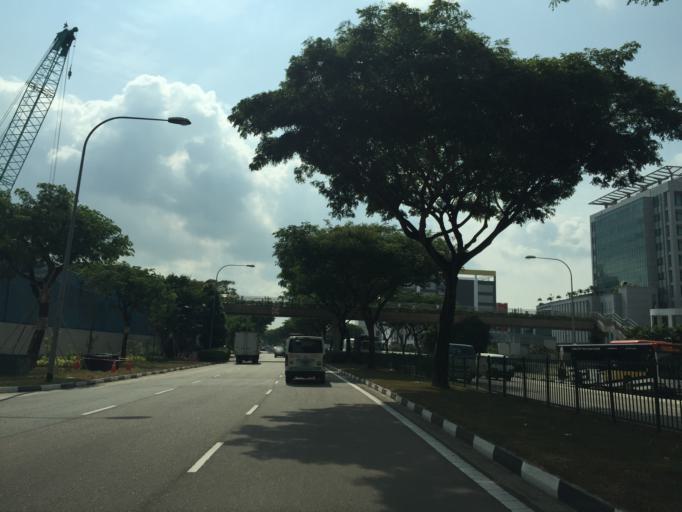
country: SG
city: Singapore
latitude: 1.3342
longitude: 103.8908
